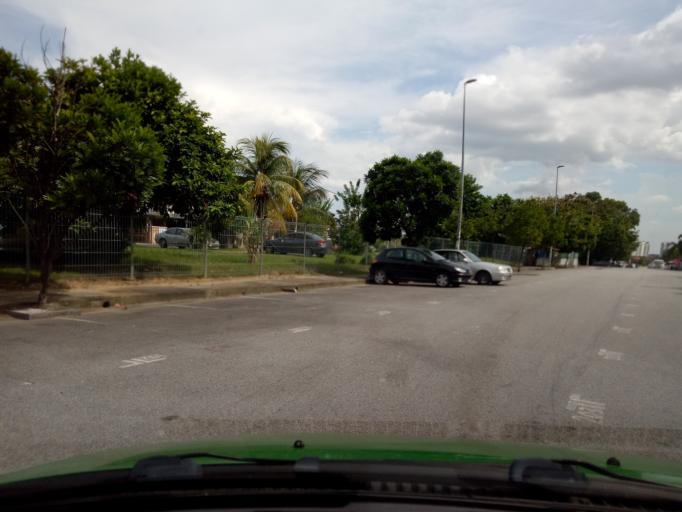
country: MY
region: Selangor
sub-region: Hulu Langat
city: Semenyih
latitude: 2.9303
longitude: 101.8590
